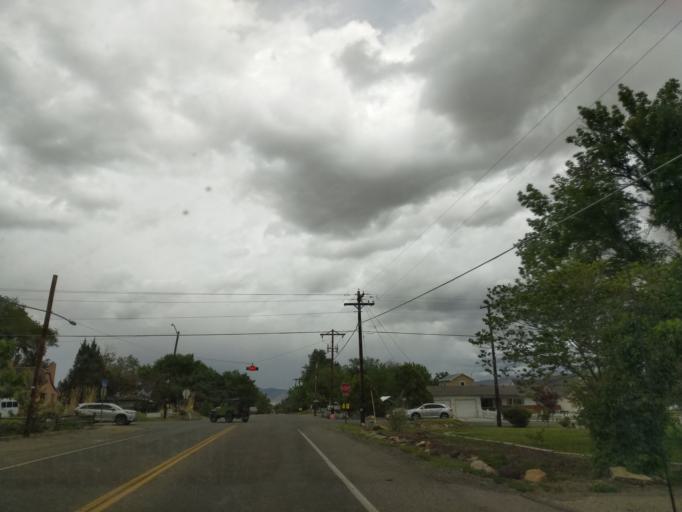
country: US
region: Colorado
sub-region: Mesa County
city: Grand Junction
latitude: 39.1058
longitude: -108.5616
